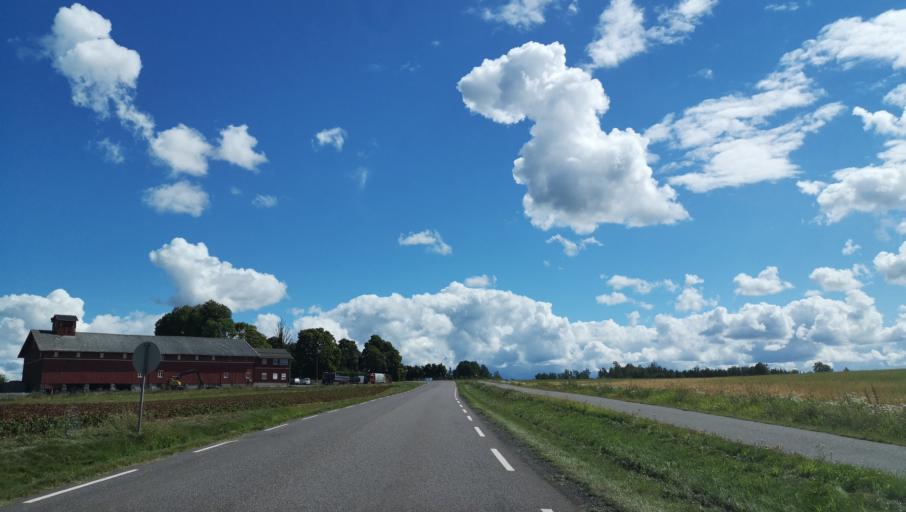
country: NO
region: Akershus
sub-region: Frogn
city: Drobak
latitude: 59.6578
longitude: 10.6893
